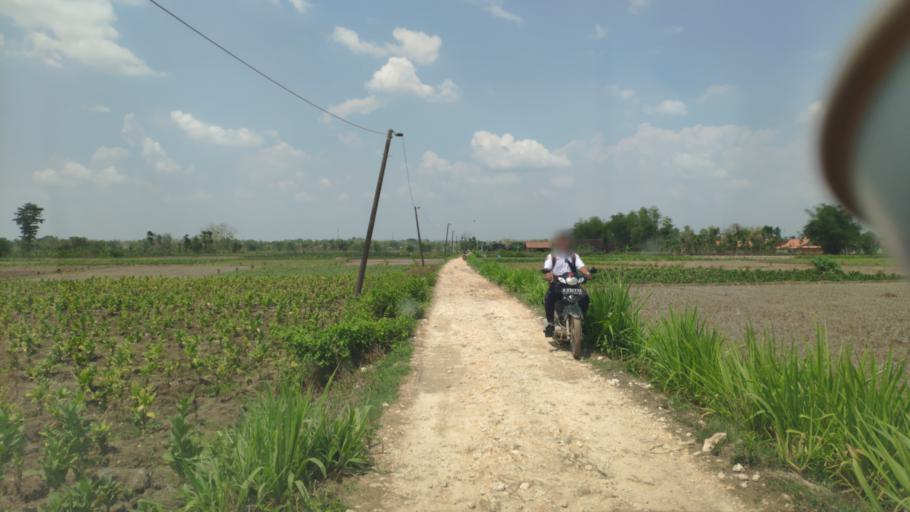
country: ID
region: Central Java
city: Sambirejo
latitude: -7.0569
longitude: 111.3433
